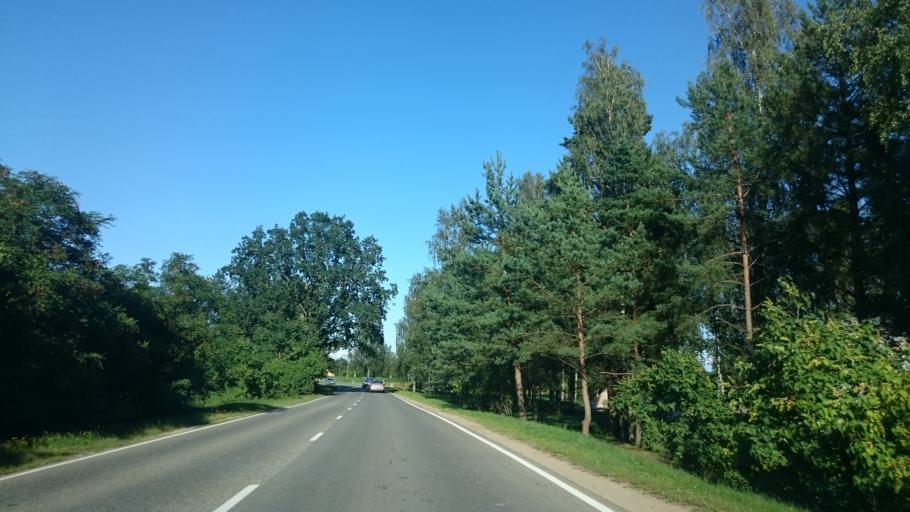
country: LV
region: Carnikava
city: Carnikava
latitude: 57.1239
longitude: 24.2719
